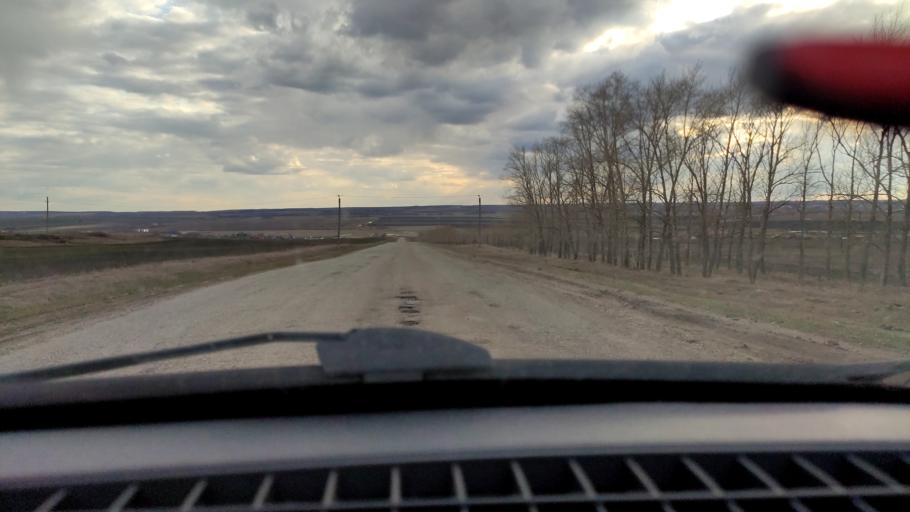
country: RU
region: Bashkortostan
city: Karmaskaly
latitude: 54.2995
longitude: 55.9237
